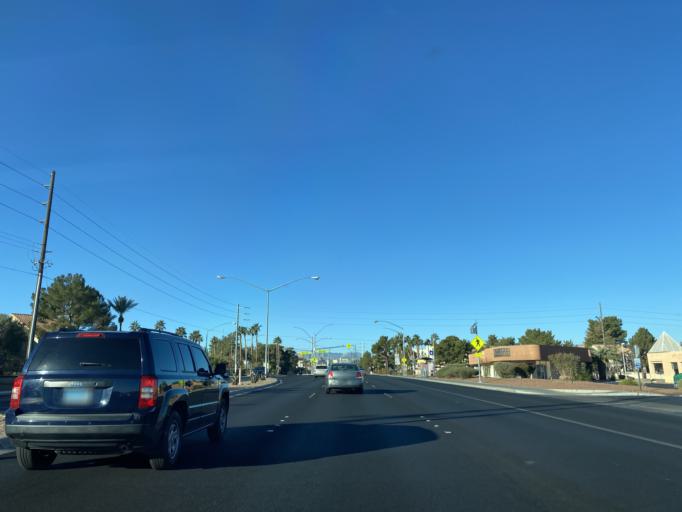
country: US
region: Nevada
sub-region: Clark County
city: Winchester
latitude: 36.1152
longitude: -115.1037
